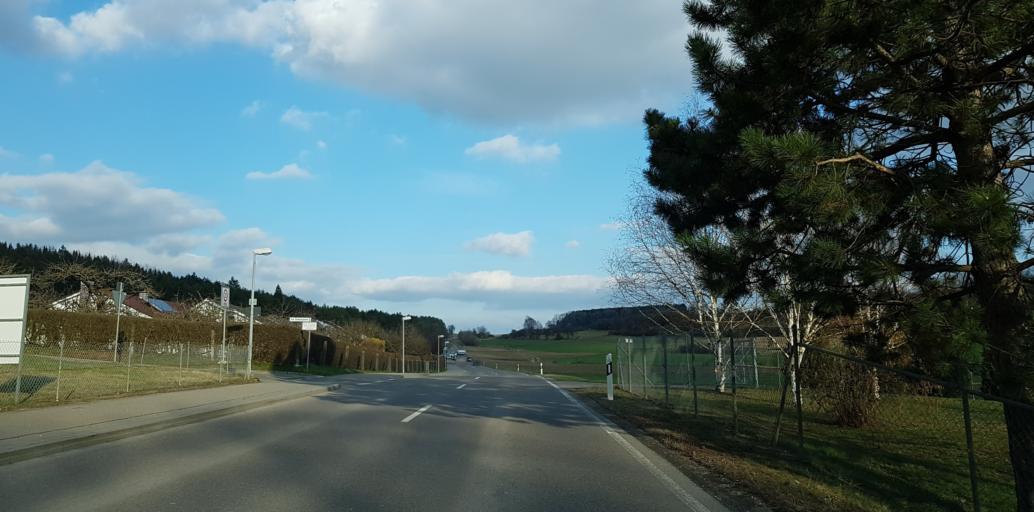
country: DE
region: Baden-Wuerttemberg
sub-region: Tuebingen Region
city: Allmendingen
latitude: 48.3239
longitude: 9.7347
